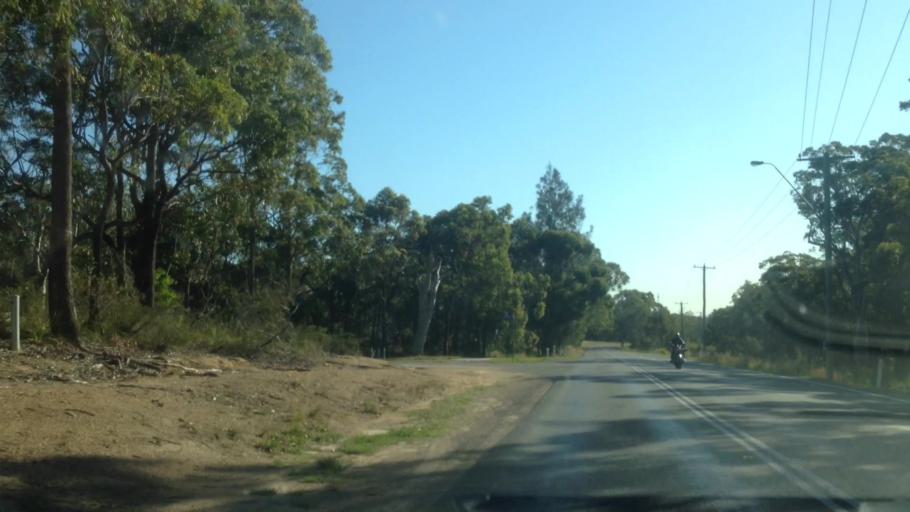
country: AU
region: New South Wales
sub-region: Lake Macquarie Shire
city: Dora Creek
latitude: -33.1076
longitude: 151.5417
